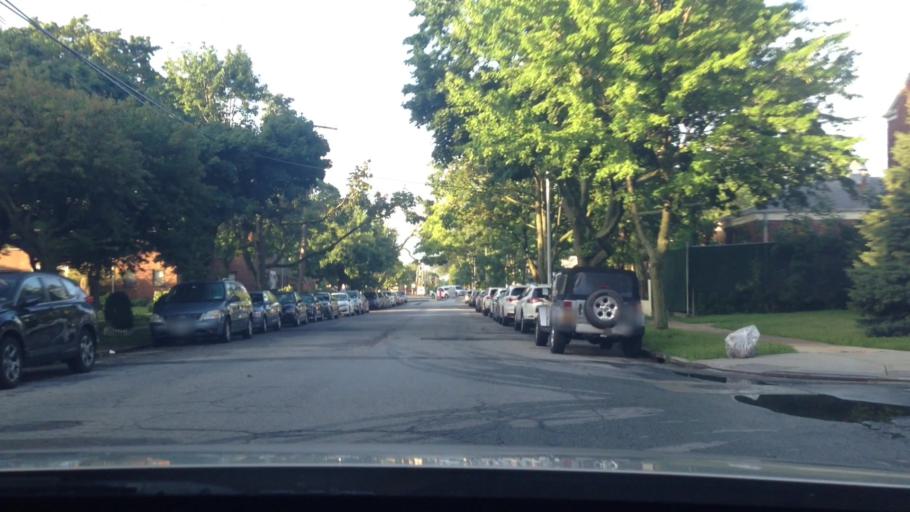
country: US
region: New York
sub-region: Nassau County
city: East Atlantic Beach
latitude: 40.7827
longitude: -73.8028
